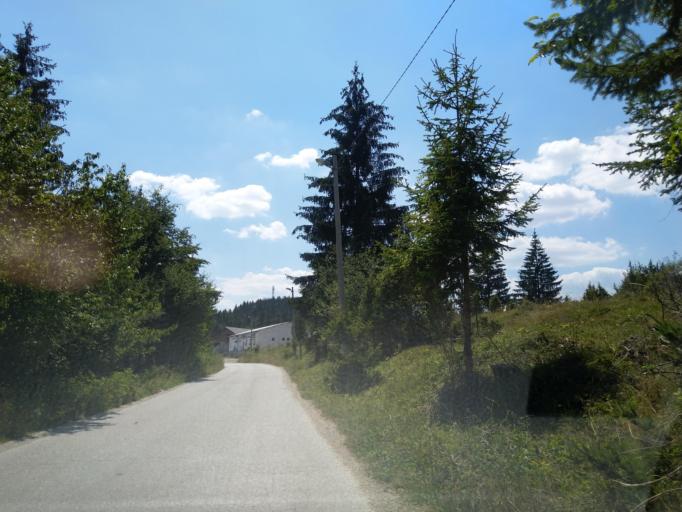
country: RS
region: Central Serbia
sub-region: Zlatiborski Okrug
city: Nova Varos
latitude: 43.4675
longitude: 19.9721
